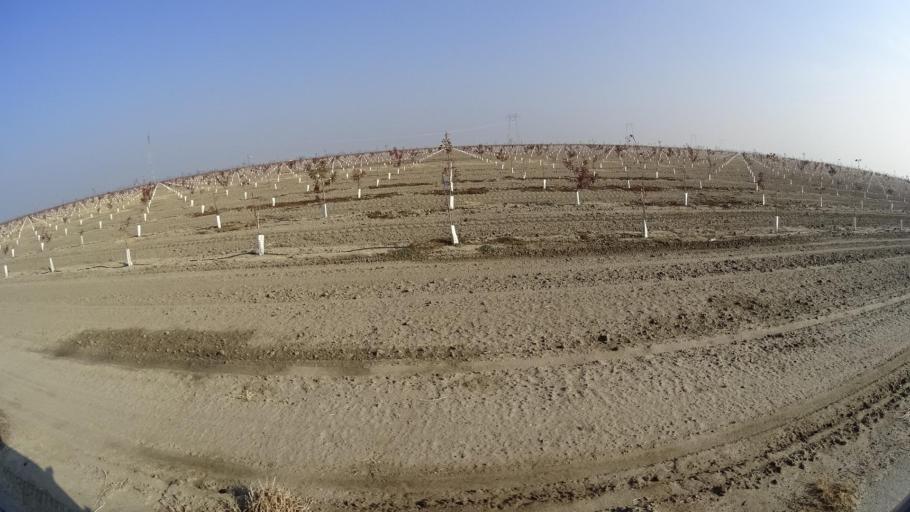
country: US
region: California
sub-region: Kern County
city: Greenfield
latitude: 35.1657
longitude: -119.0393
